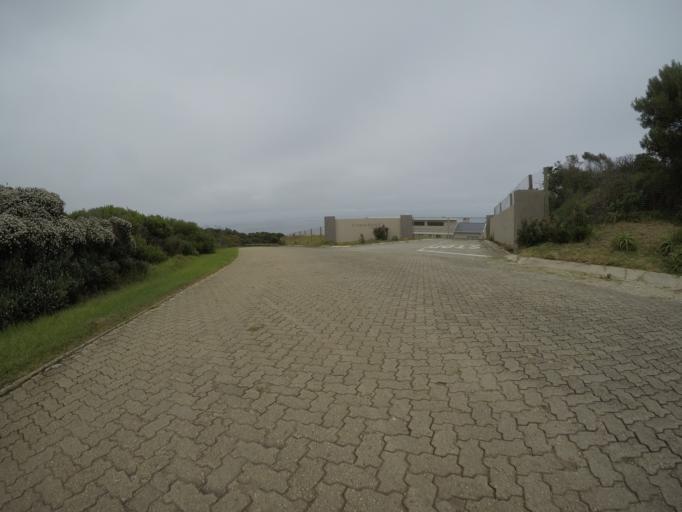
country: ZA
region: Eastern Cape
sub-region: Cacadu District Municipality
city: Kareedouw
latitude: -34.0734
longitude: 24.2326
